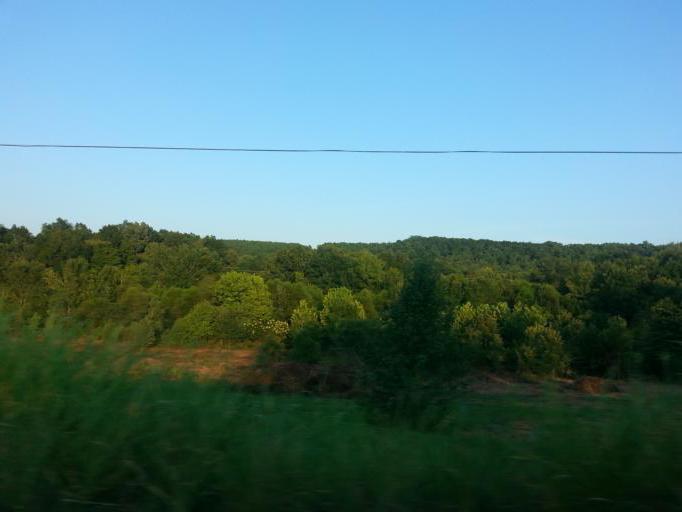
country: US
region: Tennessee
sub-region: Monroe County
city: Sweetwater
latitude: 35.5353
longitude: -84.5242
